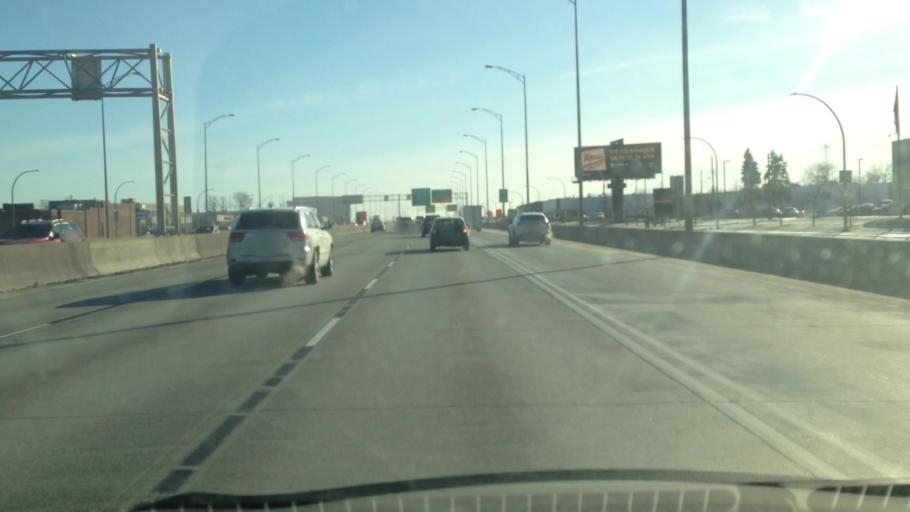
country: CA
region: Quebec
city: Dorval
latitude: 45.4973
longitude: -73.7479
